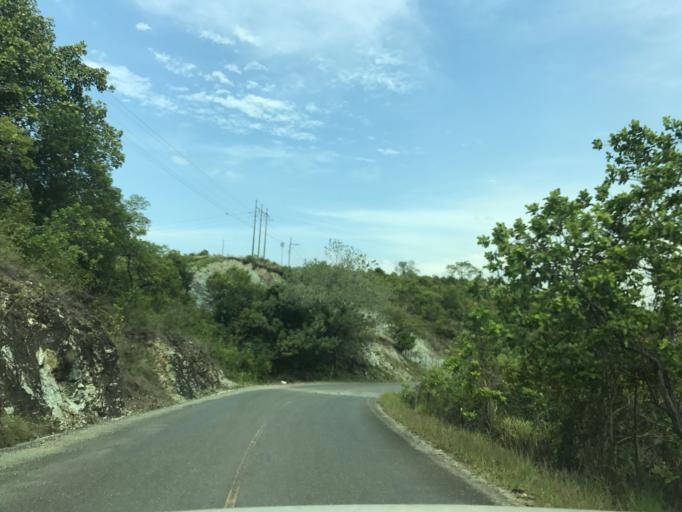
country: GT
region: Izabal
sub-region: Municipio de Los Amates
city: Los Amates
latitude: 15.3840
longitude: -89.0215
